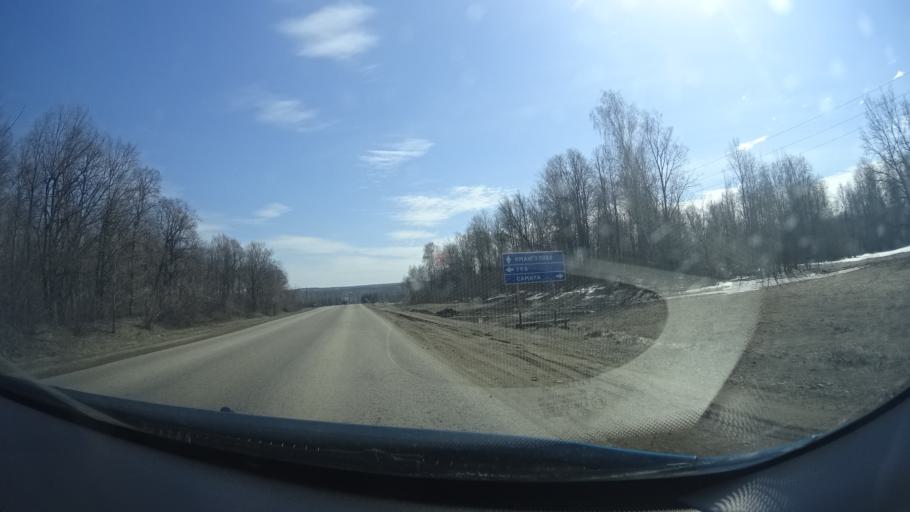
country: RU
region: Bashkortostan
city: Oktyabr'skiy
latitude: 54.4500
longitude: 53.5973
